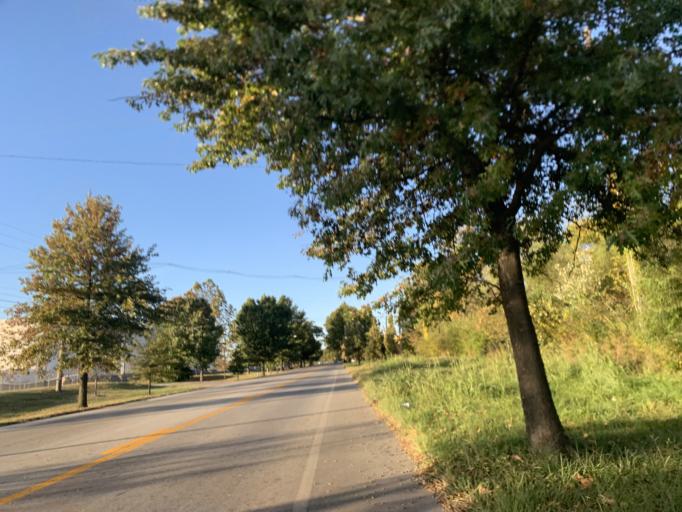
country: US
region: Kentucky
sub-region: Jefferson County
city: Shively
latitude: 38.2284
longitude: -85.8277
